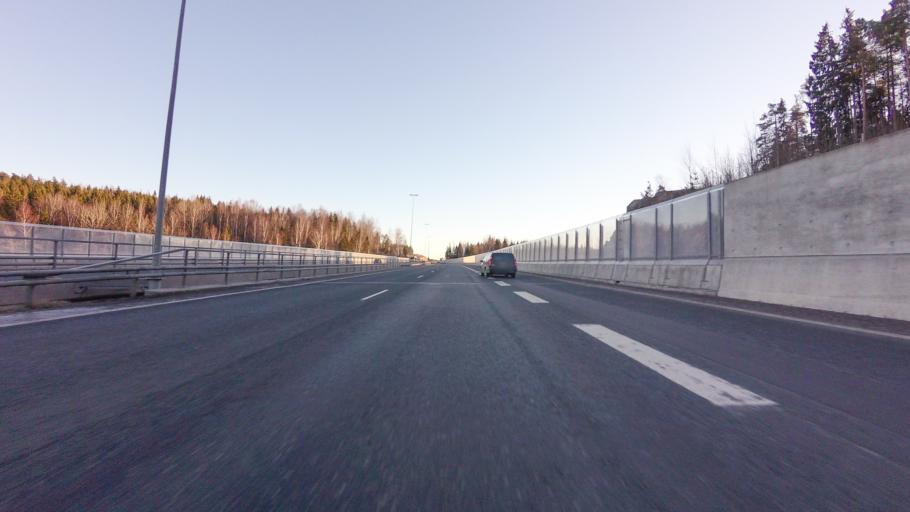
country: FI
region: Uusimaa
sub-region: Helsinki
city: Lohja
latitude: 60.2910
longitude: 24.0724
